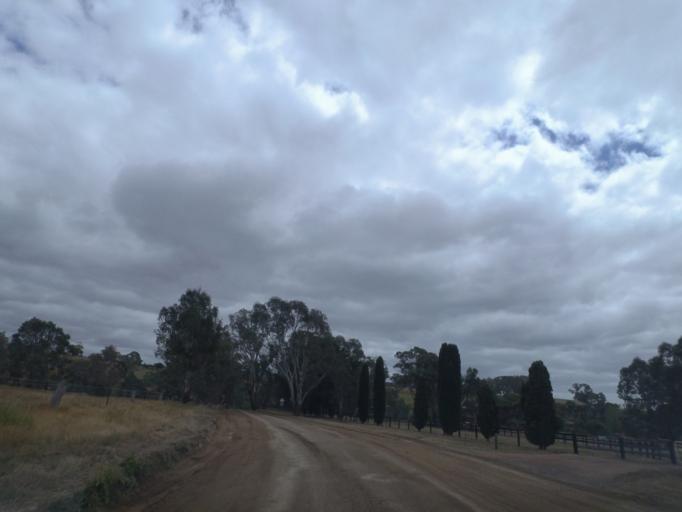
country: AU
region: Victoria
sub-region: Whittlesea
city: Whittlesea
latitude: -37.1129
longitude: 145.0244
